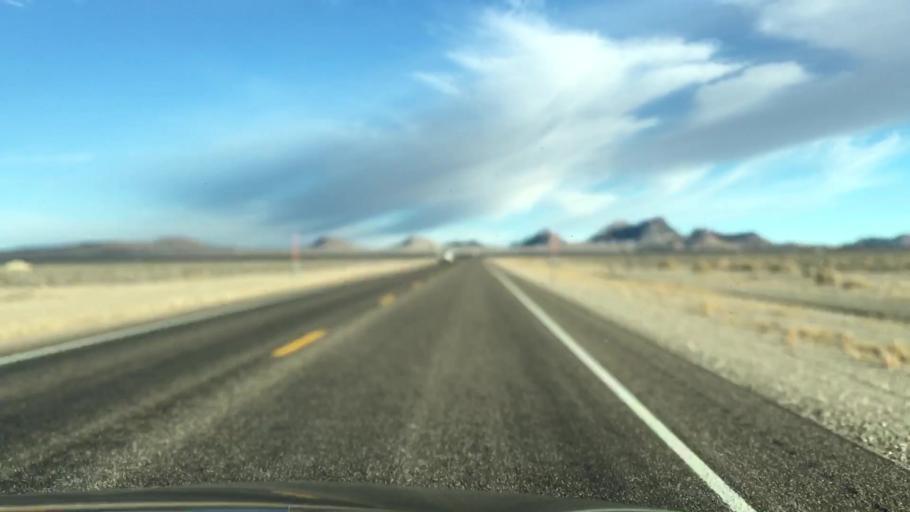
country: US
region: Nevada
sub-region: Nye County
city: Tonopah
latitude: 38.1007
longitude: -117.3307
